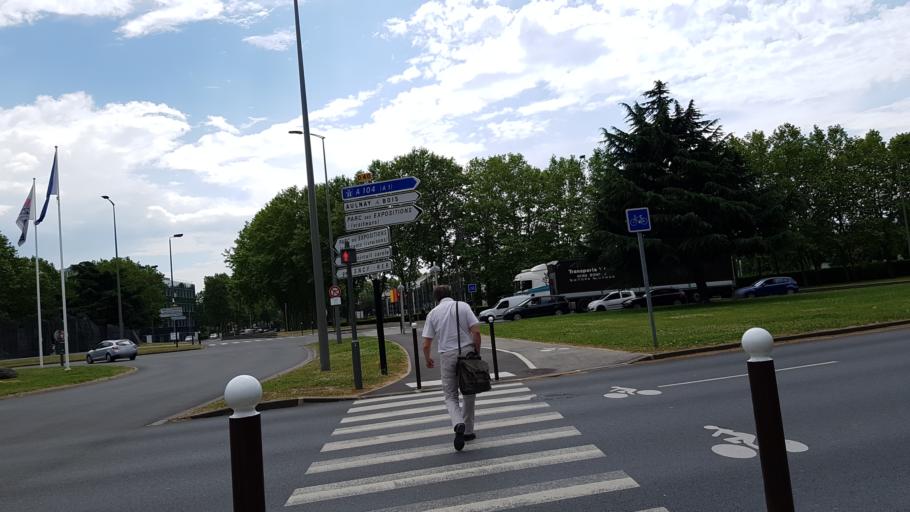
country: FR
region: Ile-de-France
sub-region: Departement de Seine-Saint-Denis
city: Villepinte
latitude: 48.9742
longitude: 2.5081
